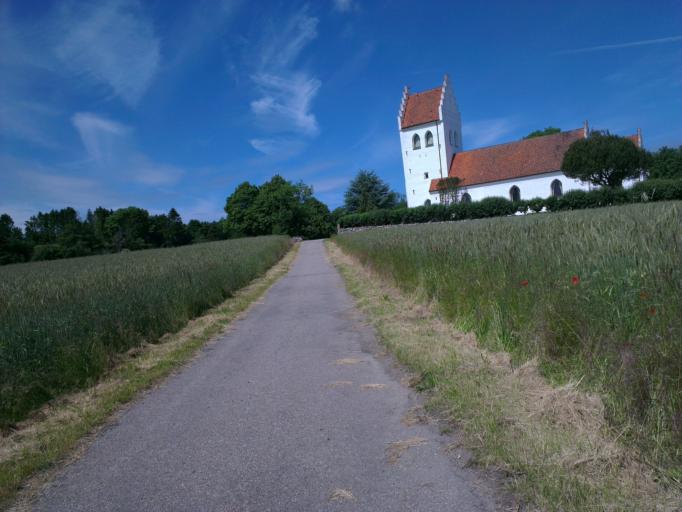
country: DK
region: Capital Region
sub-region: Frederikssund Kommune
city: Skibby
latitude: 55.7827
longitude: 11.9661
